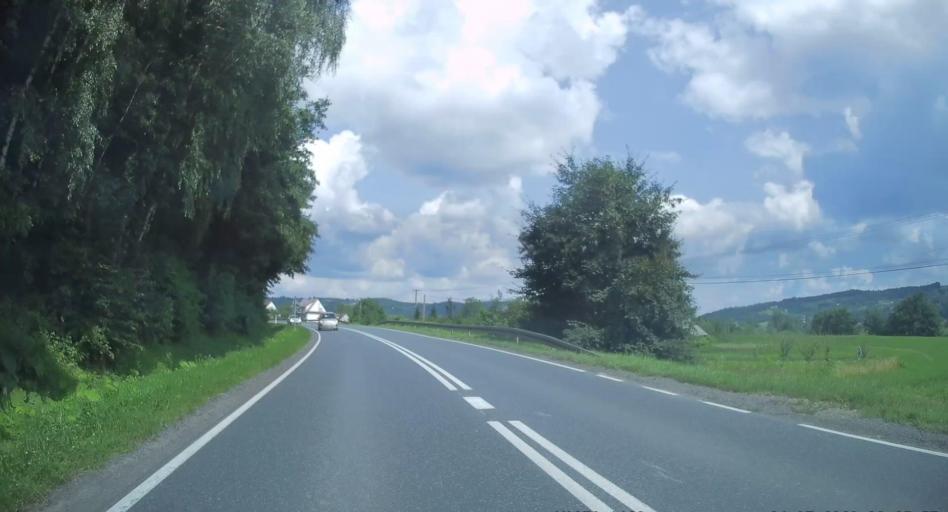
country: PL
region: Lesser Poland Voivodeship
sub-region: Powiat tarnowski
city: Janowice
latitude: 49.8857
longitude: 20.8307
